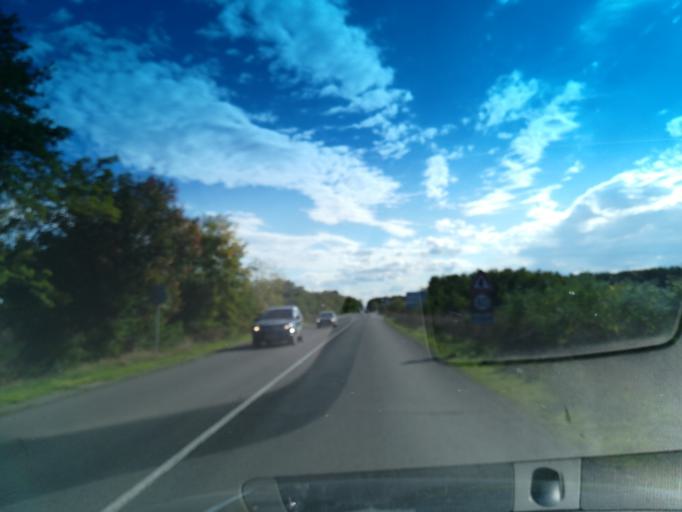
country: BG
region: Stara Zagora
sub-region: Obshtina Stara Zagora
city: Stara Zagora
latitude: 42.3590
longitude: 25.6564
